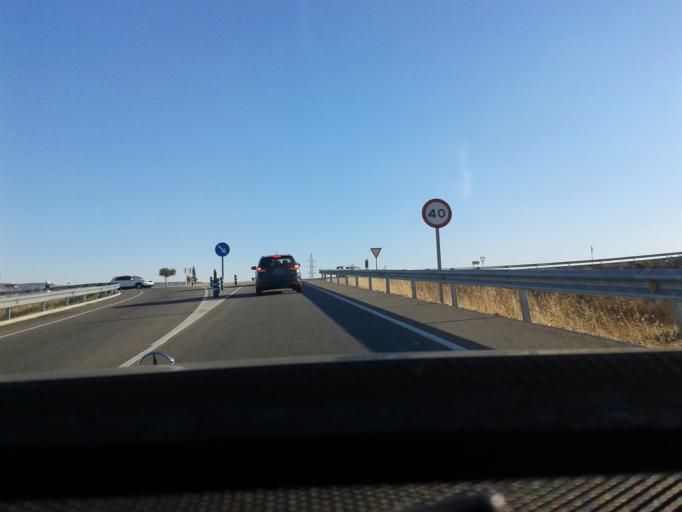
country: ES
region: Castille-La Mancha
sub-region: Provincia de Guadalajara
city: Quer
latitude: 40.5871
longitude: -3.2715
